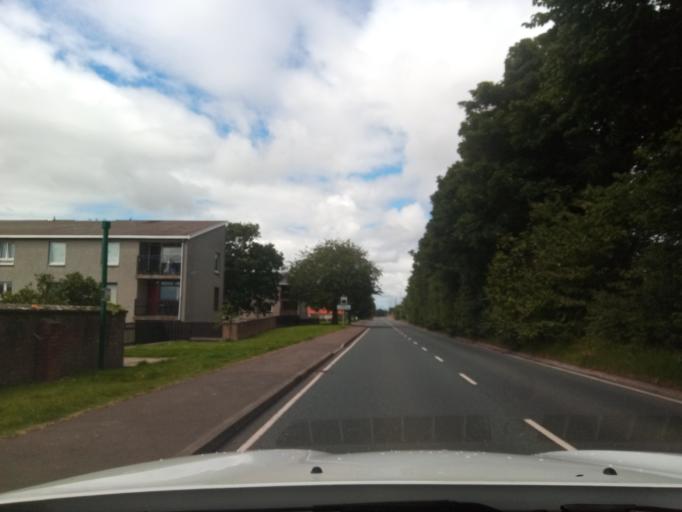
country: GB
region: Scotland
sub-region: Fife
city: Kincardine
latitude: 56.0671
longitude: -3.7076
